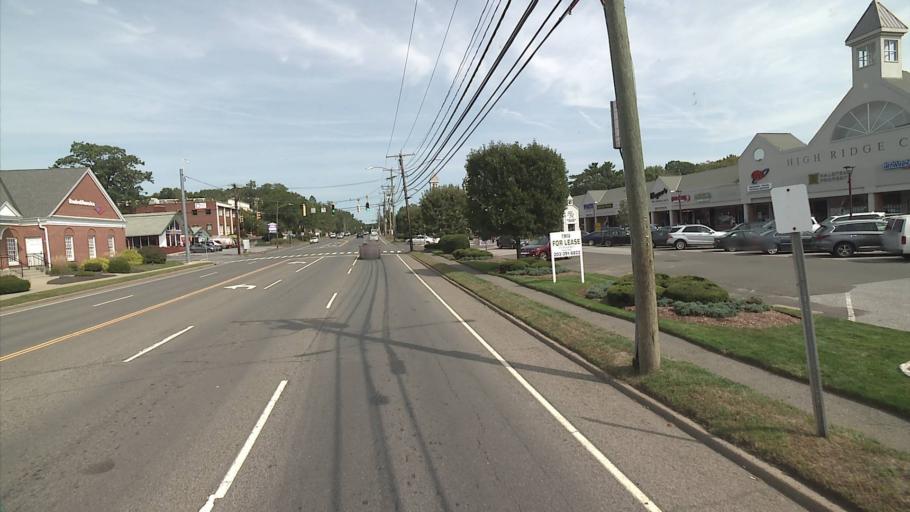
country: US
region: Connecticut
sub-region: Fairfield County
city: North Stamford
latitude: 41.1080
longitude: -73.5476
